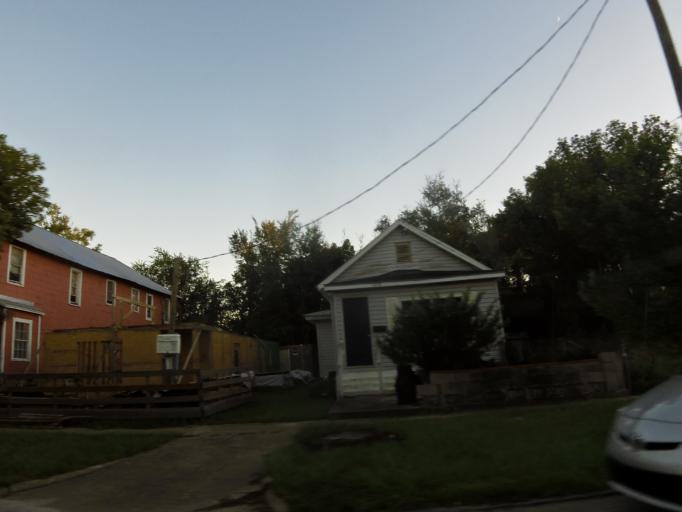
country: US
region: Florida
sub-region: Duval County
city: Jacksonville
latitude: 30.3336
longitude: -81.6419
